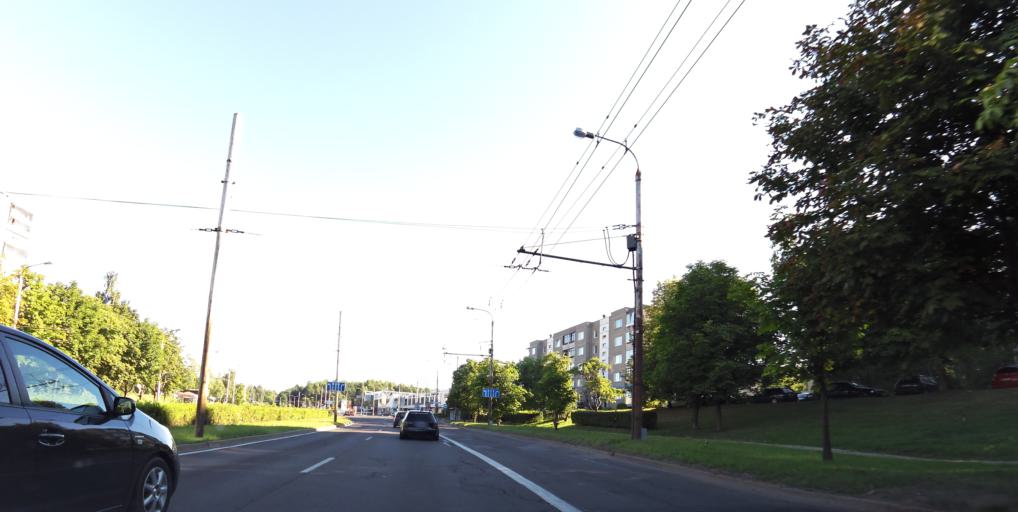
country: LT
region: Vilnius County
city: Justiniskes
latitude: 54.7057
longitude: 25.2263
